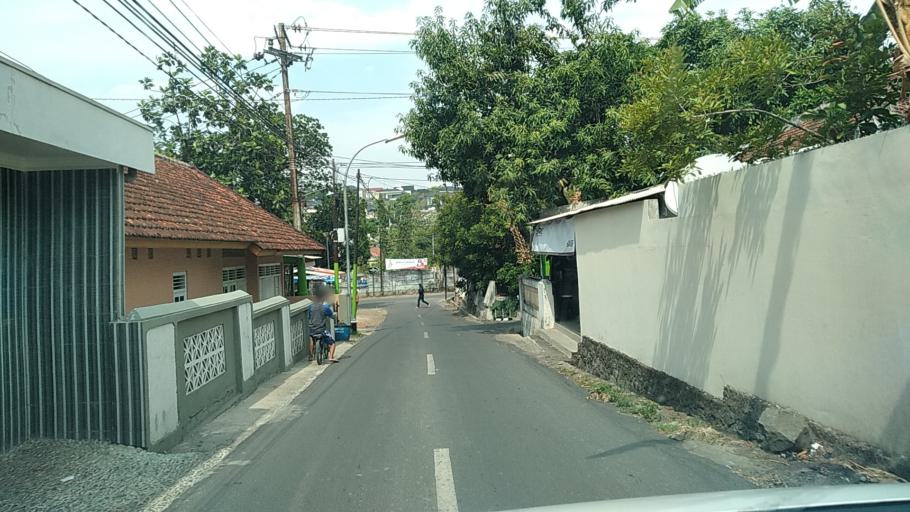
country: ID
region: Central Java
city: Semarang
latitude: -7.0337
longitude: 110.4310
